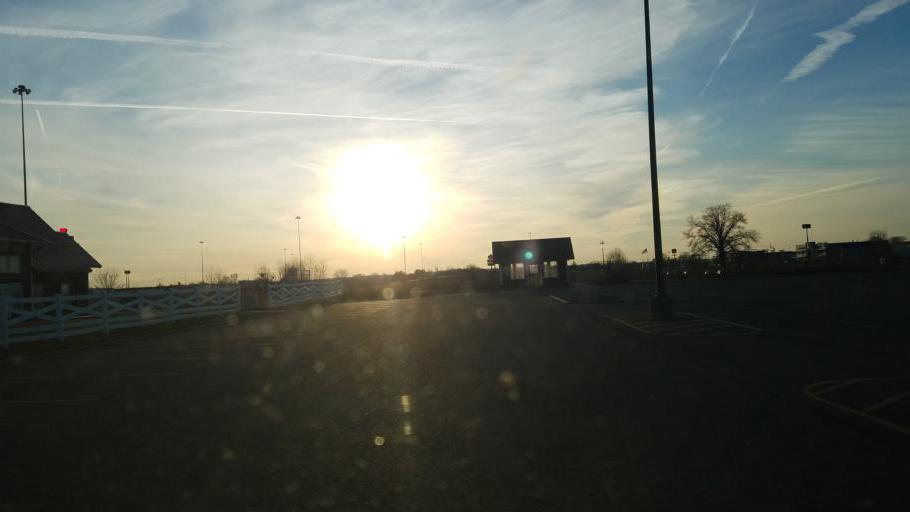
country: US
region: Ohio
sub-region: Medina County
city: Lodi
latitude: 40.9986
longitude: -81.9889
